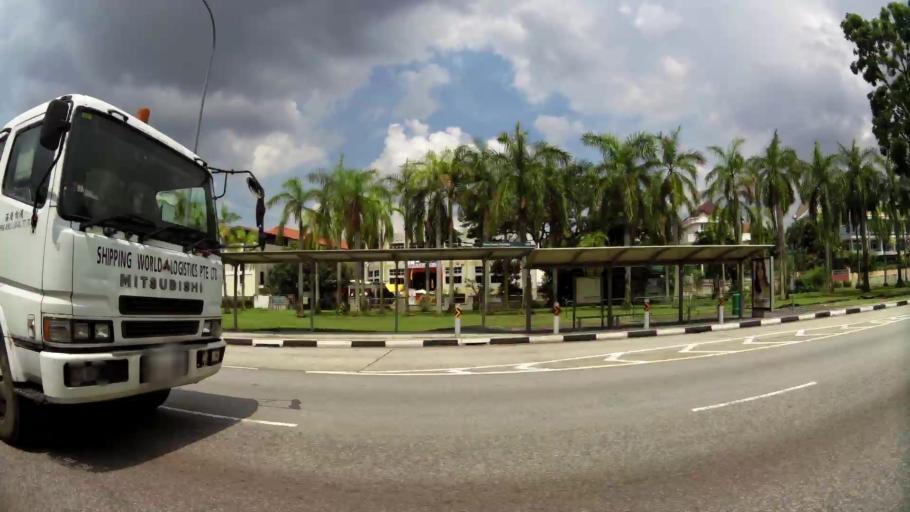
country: SG
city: Singapore
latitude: 1.2892
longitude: 103.7740
